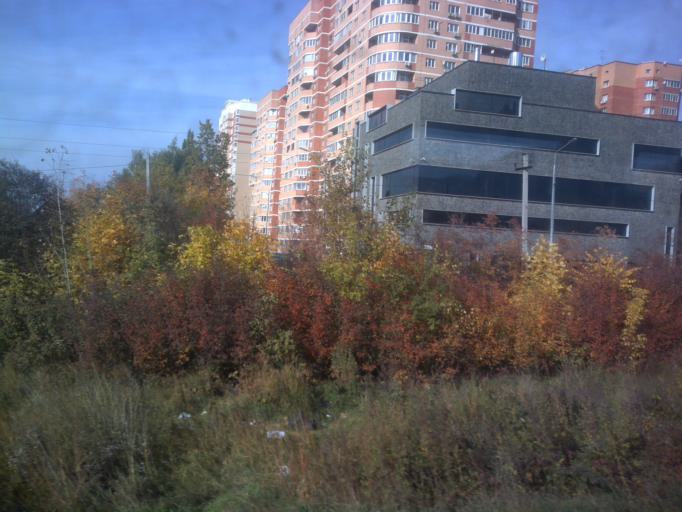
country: RU
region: Moskovskaya
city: Shcherbinka
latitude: 55.5017
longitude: 37.5594
